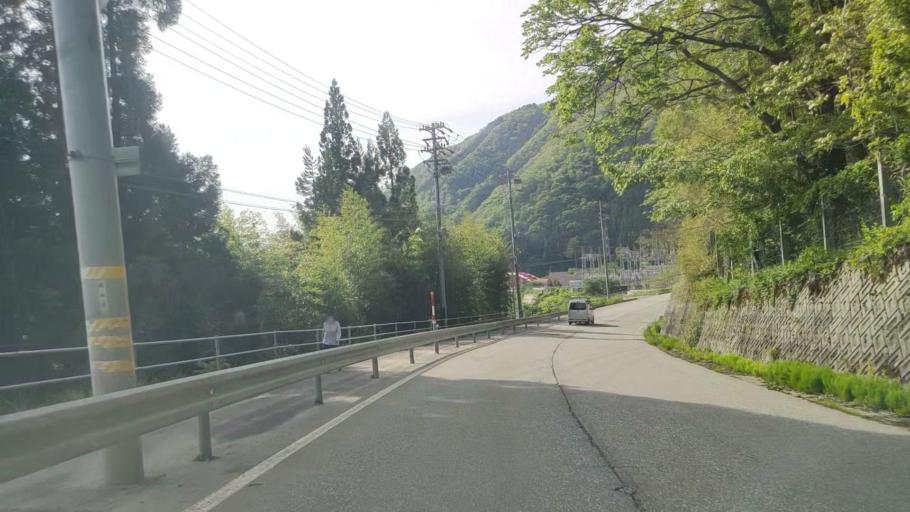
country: JP
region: Gifu
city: Takayama
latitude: 36.2924
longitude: 137.3725
